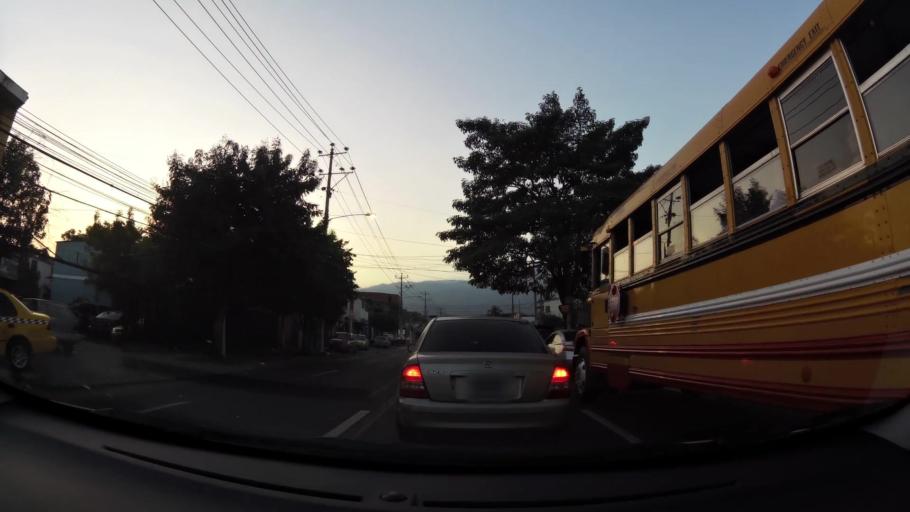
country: SV
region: San Salvador
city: Mejicanos
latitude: 13.7158
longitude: -89.2161
